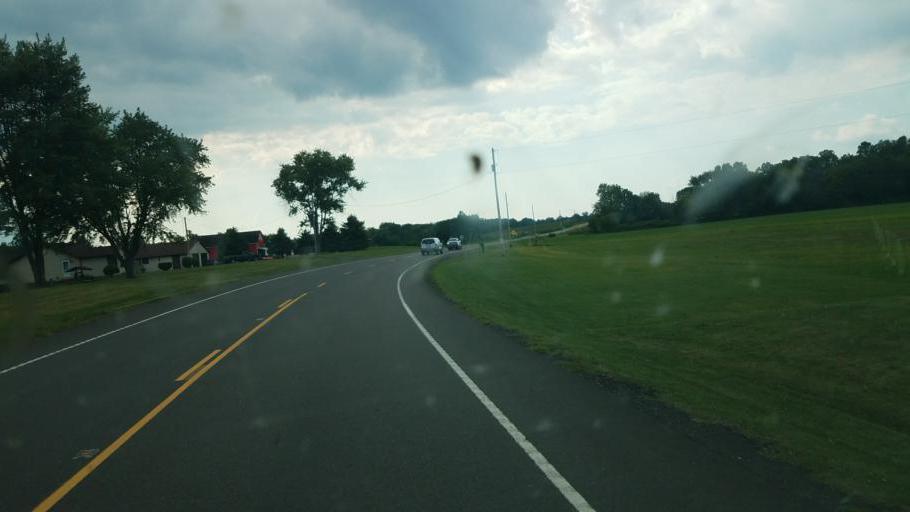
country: US
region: Ohio
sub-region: Knox County
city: Fredericktown
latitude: 40.4636
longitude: -82.6342
